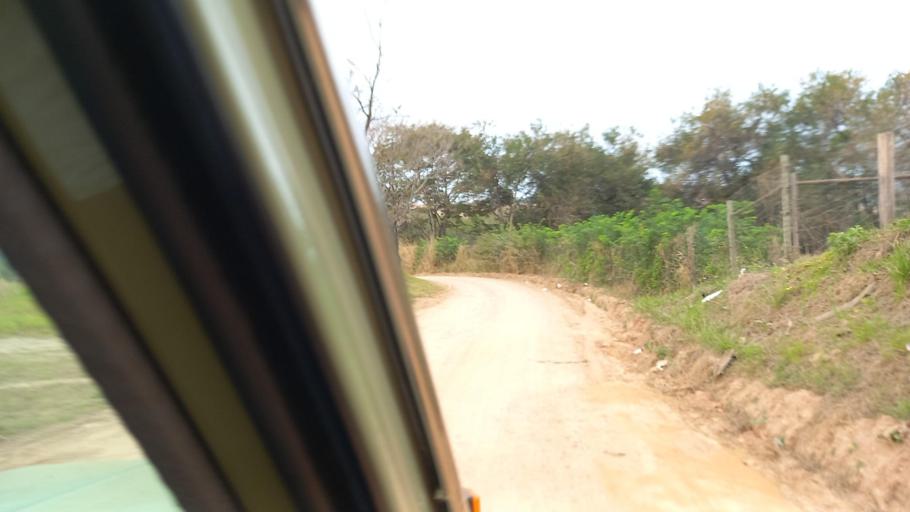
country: BR
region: Sao Paulo
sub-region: Moji-Guacu
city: Mogi-Gaucu
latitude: -22.2730
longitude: -46.8479
